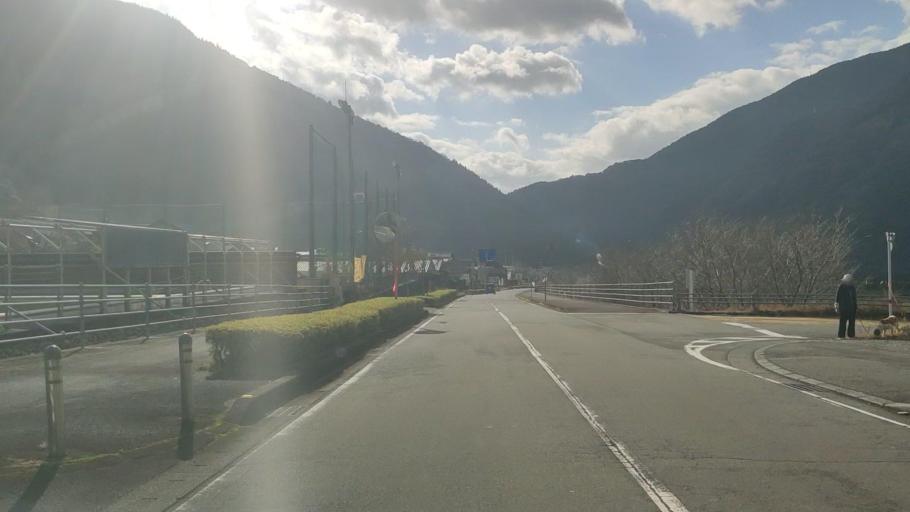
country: JP
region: Kumamoto
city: Hitoyoshi
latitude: 32.4018
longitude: 130.8261
